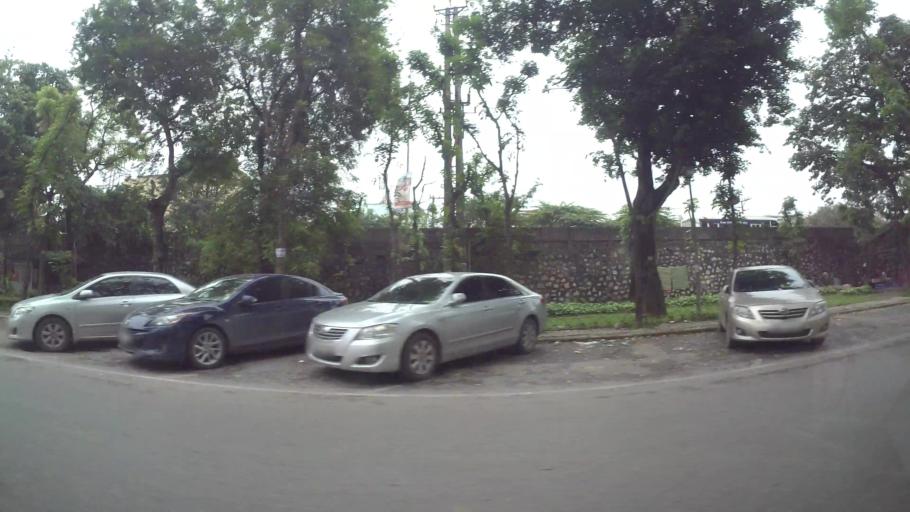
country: VN
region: Ha Noi
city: Hai BaTrung
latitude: 21.0168
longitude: 105.8622
